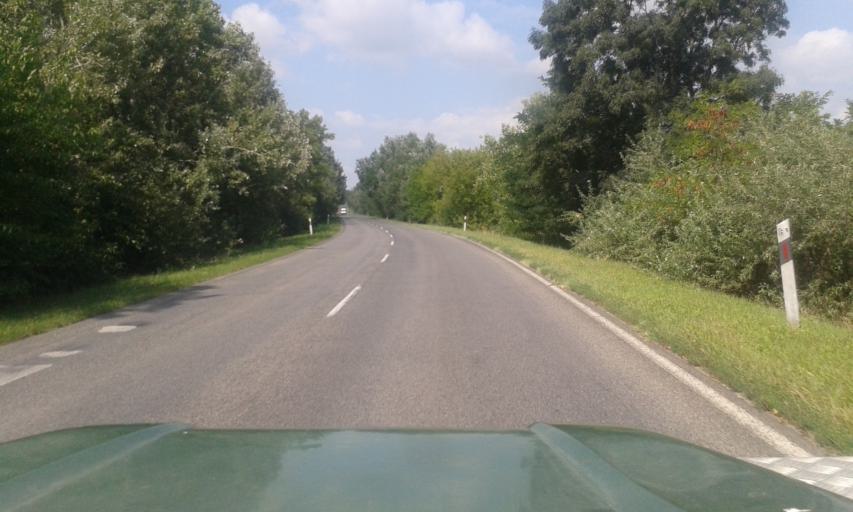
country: HU
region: Csongrad
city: Szatymaz
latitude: 46.3414
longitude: 20.0654
